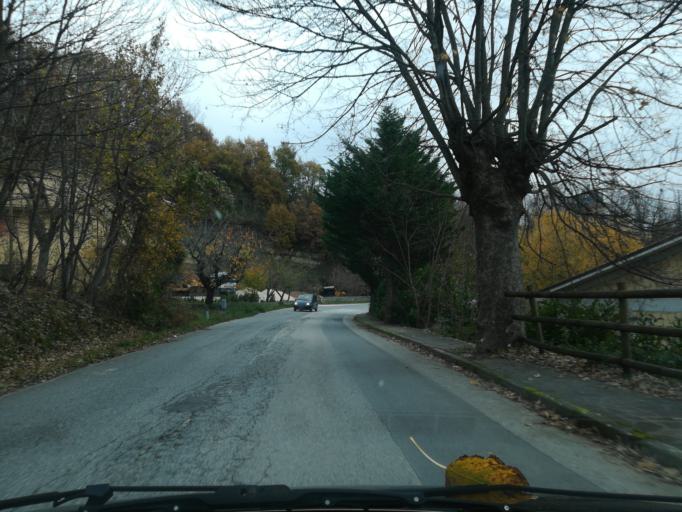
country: IT
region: Molise
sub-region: Provincia di Isernia
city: Agnone
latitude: 41.8150
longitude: 14.3740
